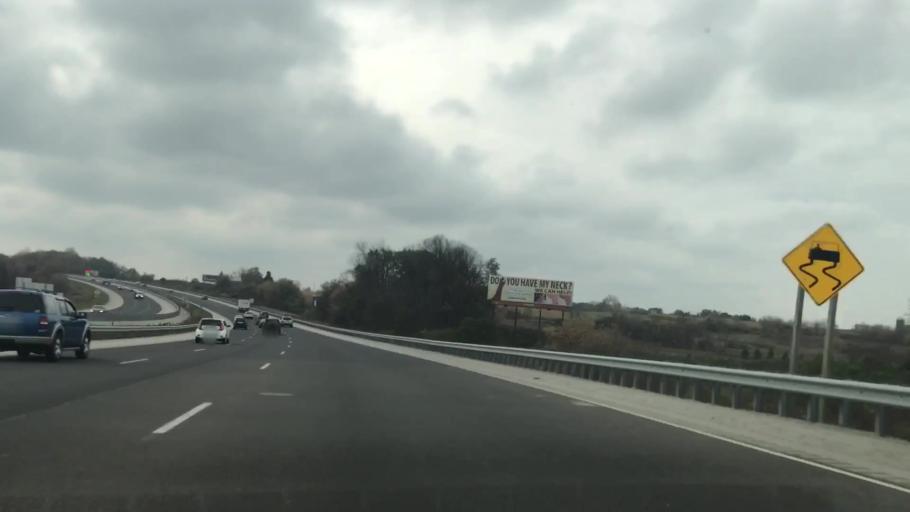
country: US
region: Wisconsin
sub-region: Washington County
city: Richfield
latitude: 43.2469
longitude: -88.1818
